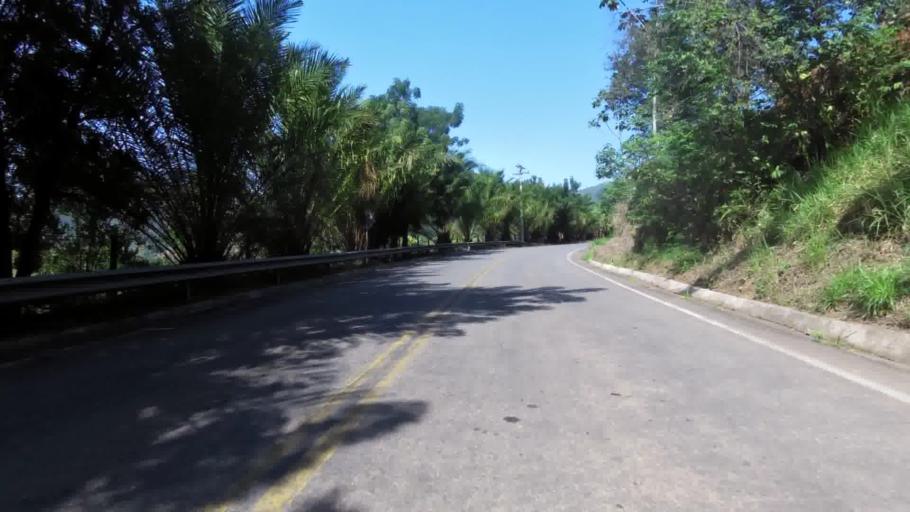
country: BR
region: Espirito Santo
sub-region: Alfredo Chaves
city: Alfredo Chaves
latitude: -20.6144
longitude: -40.7790
